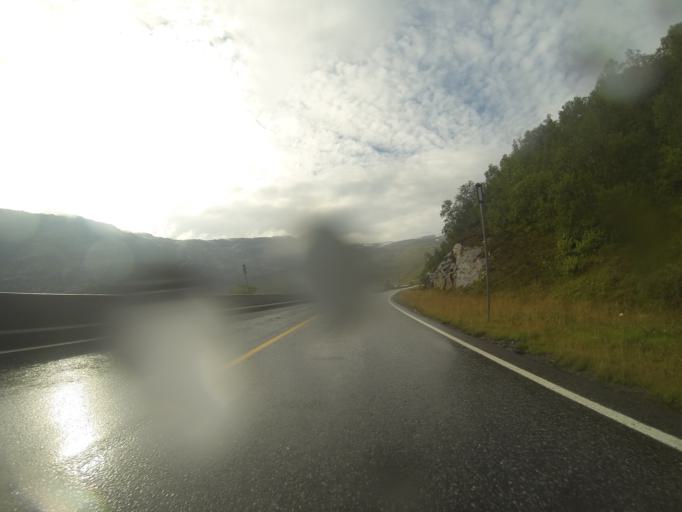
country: NO
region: Hordaland
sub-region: Odda
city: Odda
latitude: 59.8203
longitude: 6.7492
